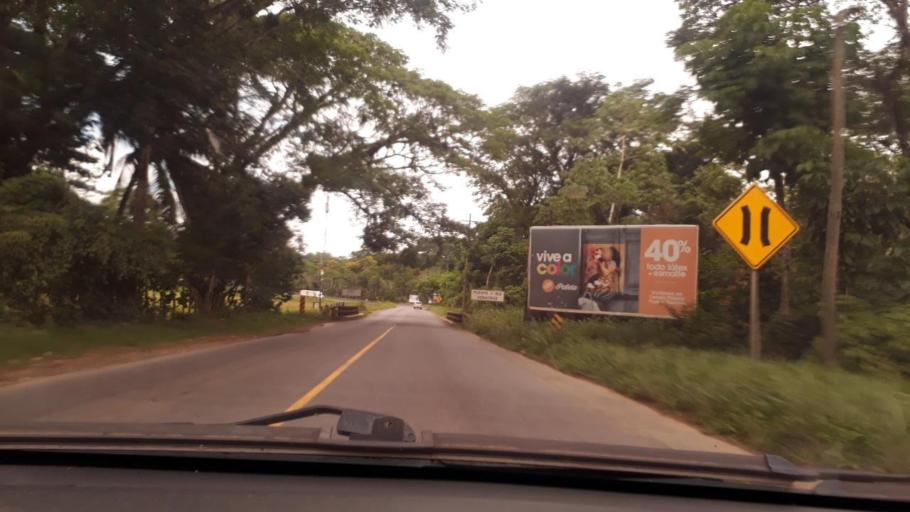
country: GT
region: Izabal
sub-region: Municipio de Puerto Barrios
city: Puerto Barrios
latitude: 15.6205
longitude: -88.5625
